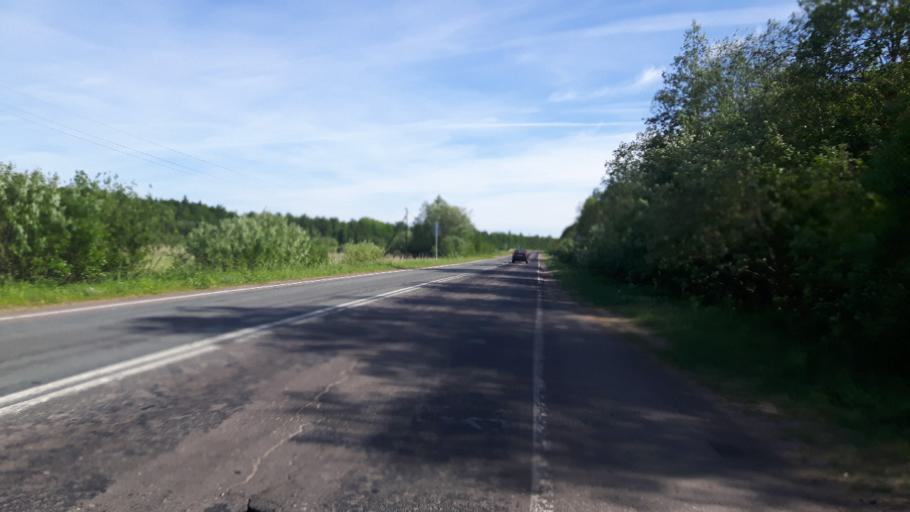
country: RU
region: Leningrad
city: Ivangorod
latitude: 59.4142
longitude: 28.3822
